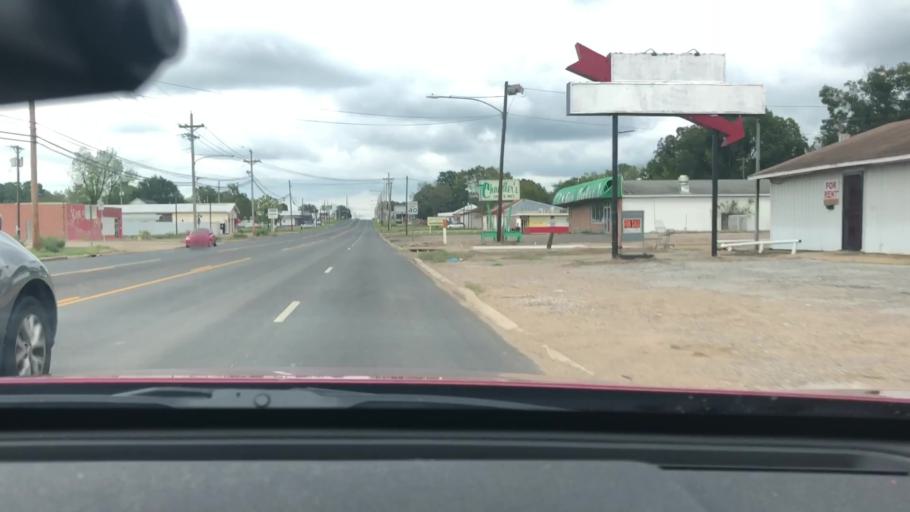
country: US
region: Arkansas
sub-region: Miller County
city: Texarkana
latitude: 33.4307
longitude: -94.0221
